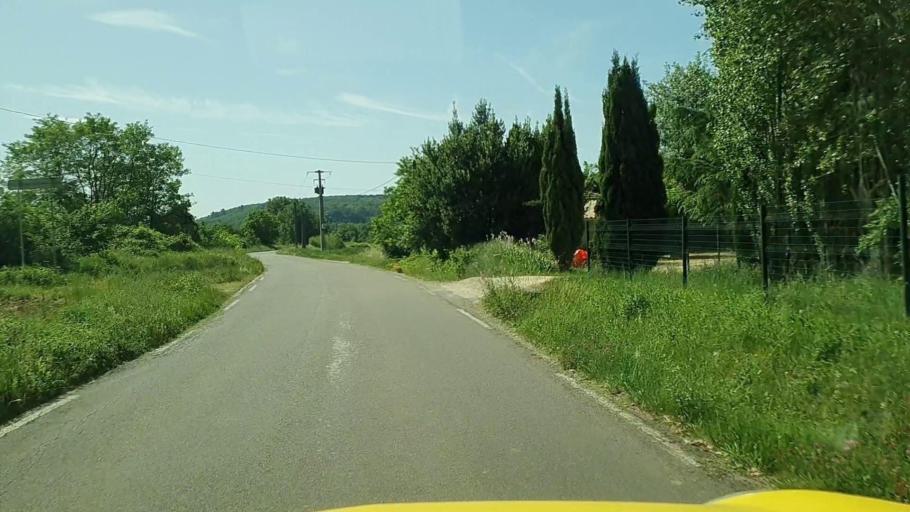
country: FR
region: Languedoc-Roussillon
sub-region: Departement du Gard
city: Tresques
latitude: 44.1025
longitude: 4.5443
